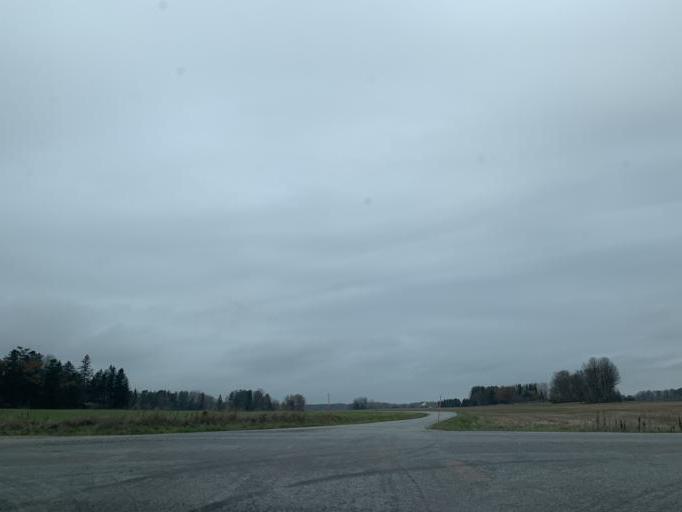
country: SE
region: Vaestmanland
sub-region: Vasteras
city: Skultuna
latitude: 59.7006
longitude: 16.4178
